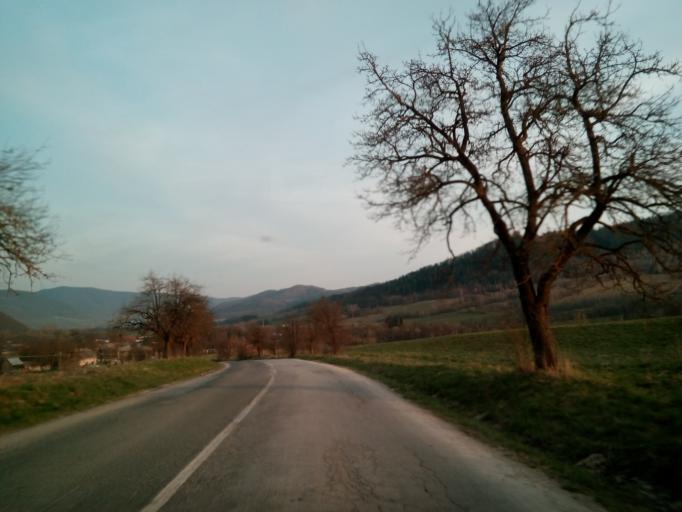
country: SK
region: Kosicky
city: Dobsina
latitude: 48.7071
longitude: 20.2923
